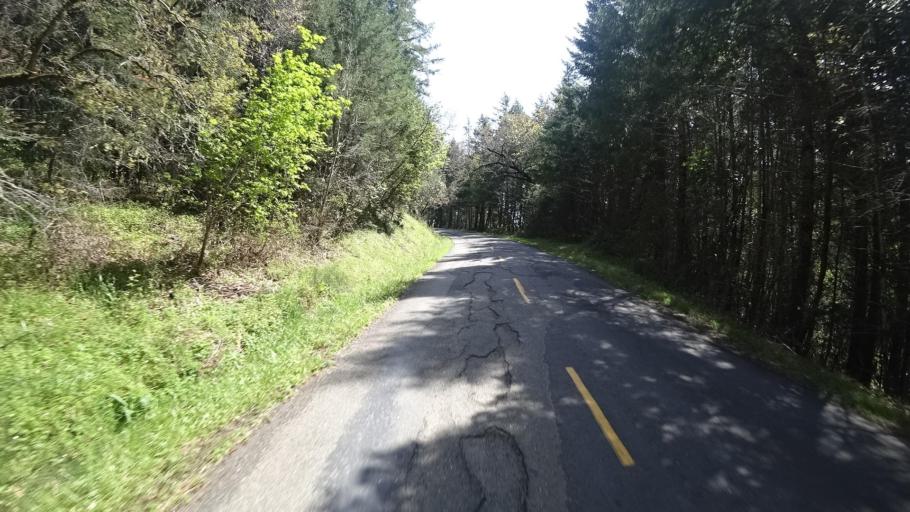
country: US
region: California
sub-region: Humboldt County
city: Redway
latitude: 40.3172
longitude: -123.6605
